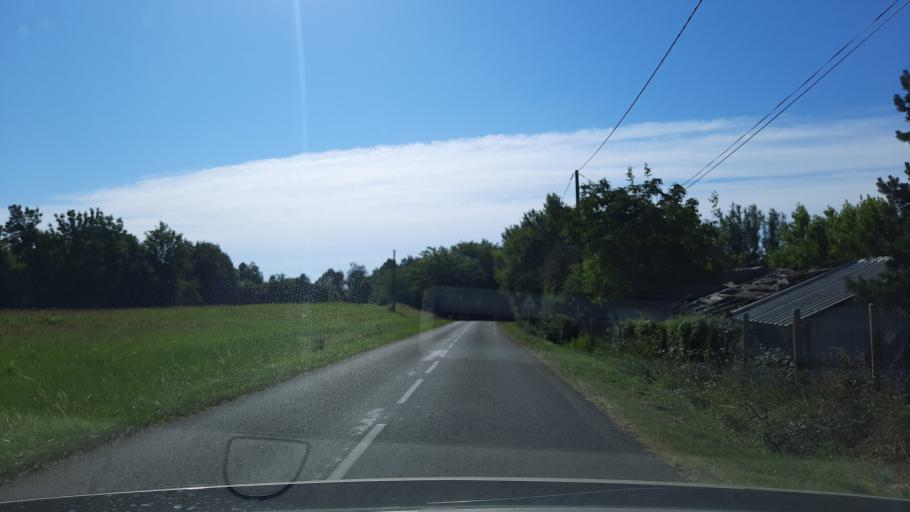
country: FR
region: Midi-Pyrenees
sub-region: Departement du Tarn-et-Garonne
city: Molieres
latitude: 44.2021
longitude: 1.4116
